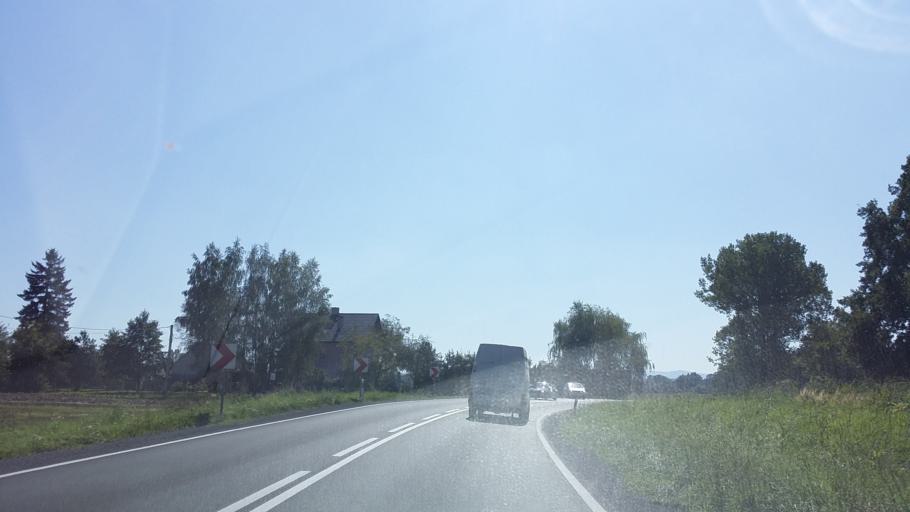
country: PL
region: Lesser Poland Voivodeship
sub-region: Powiat oswiecimski
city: Zator
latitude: 49.9690
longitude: 19.4411
